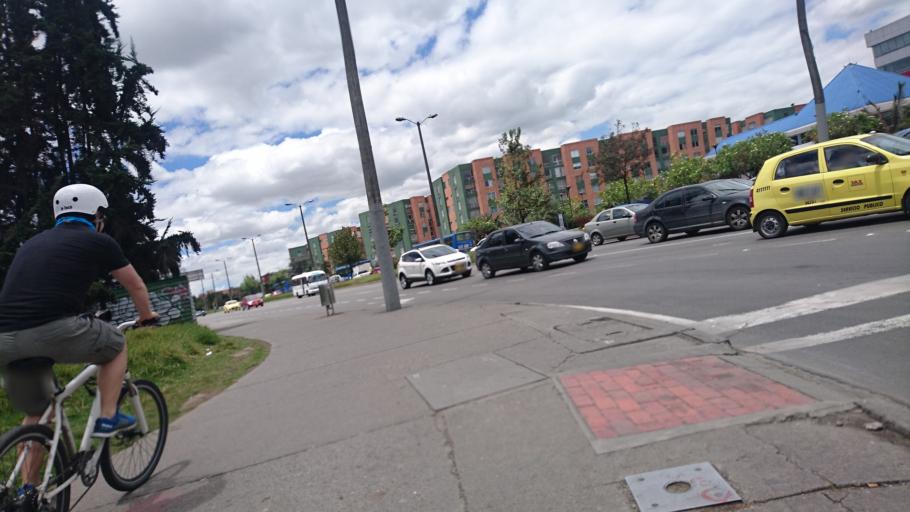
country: CO
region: Bogota D.C.
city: Bogota
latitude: 4.6718
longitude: -74.1253
